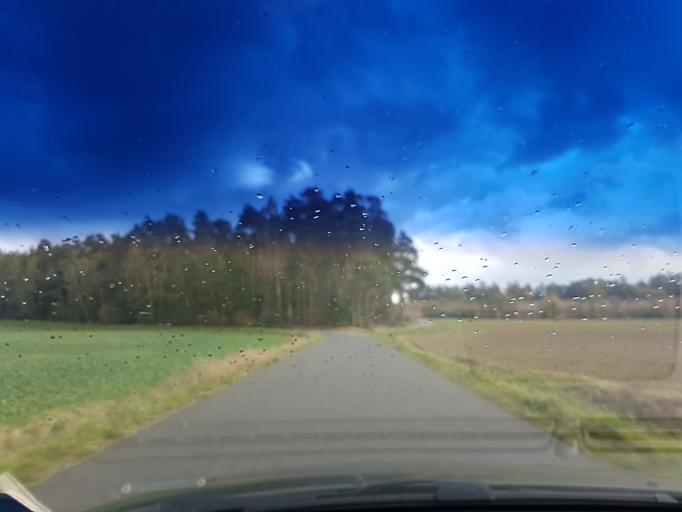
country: DE
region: Bavaria
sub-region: Regierungsbezirk Mittelfranken
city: Burghaslach
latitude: 49.7556
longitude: 10.5728
